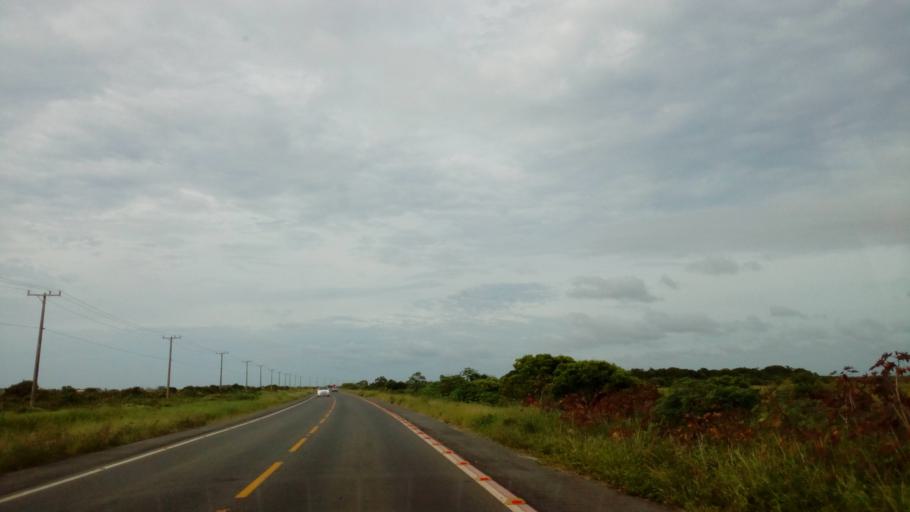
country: BR
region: Santa Catarina
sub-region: Laguna
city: Laguna
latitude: -28.5791
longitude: -48.8251
